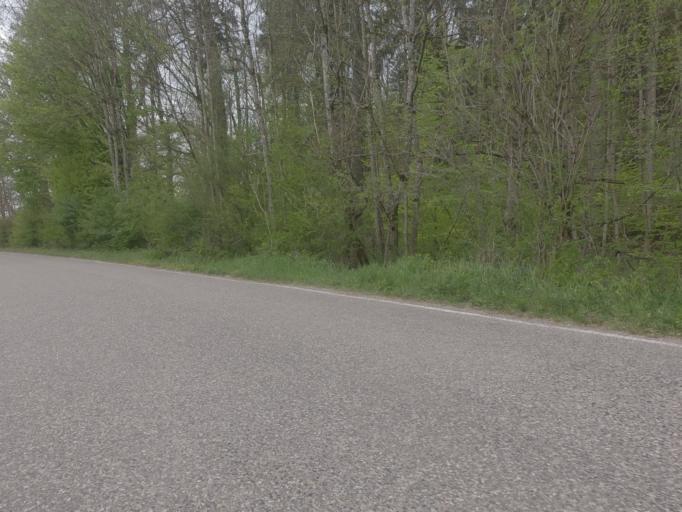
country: CH
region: Solothurn
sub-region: Bezirk Lebern
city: Riedholz
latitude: 47.2259
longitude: 7.5489
